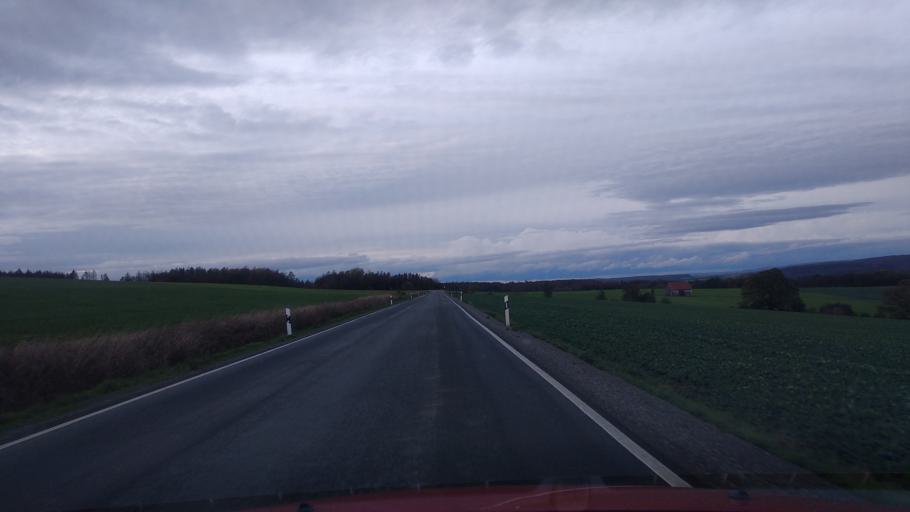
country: DE
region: North Rhine-Westphalia
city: Borgentreich
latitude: 51.6631
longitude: 9.2669
